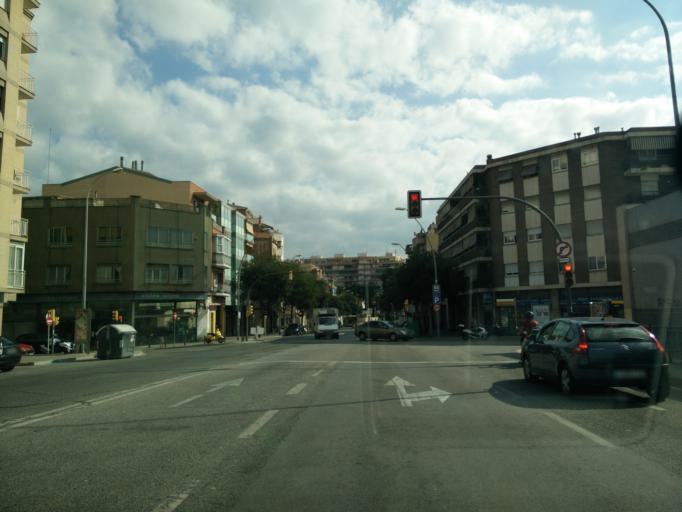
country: ES
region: Catalonia
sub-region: Provincia de Barcelona
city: Sant Adria de Besos
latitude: 41.4315
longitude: 2.2148
